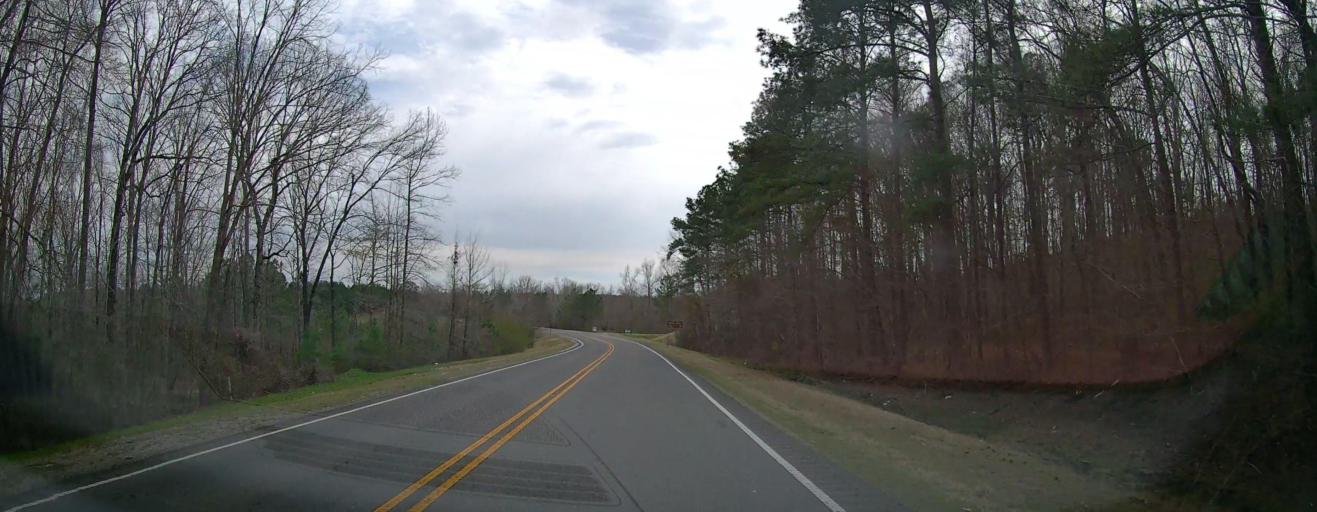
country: US
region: Alabama
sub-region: Marion County
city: Hamilton
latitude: 34.0524
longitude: -87.9656
